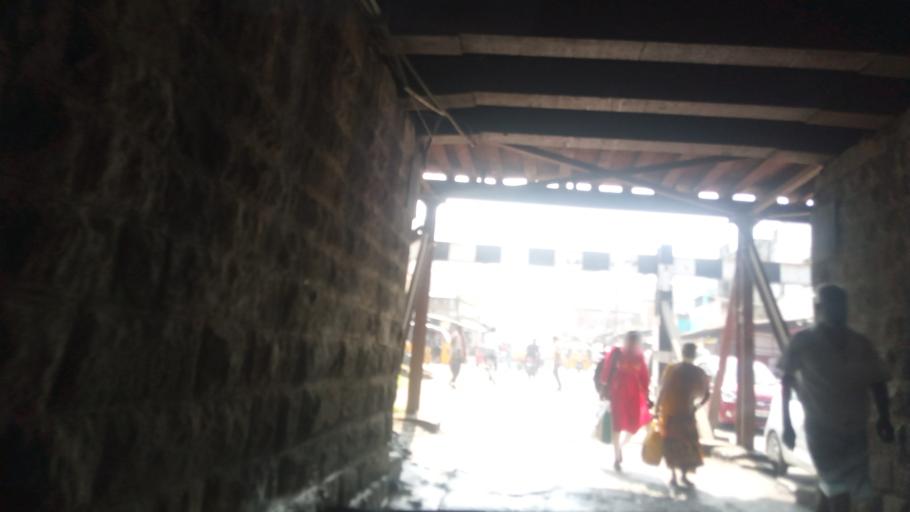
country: IN
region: Tamil Nadu
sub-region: Vellore
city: Arakkonam
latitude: 13.0822
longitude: 79.6709
